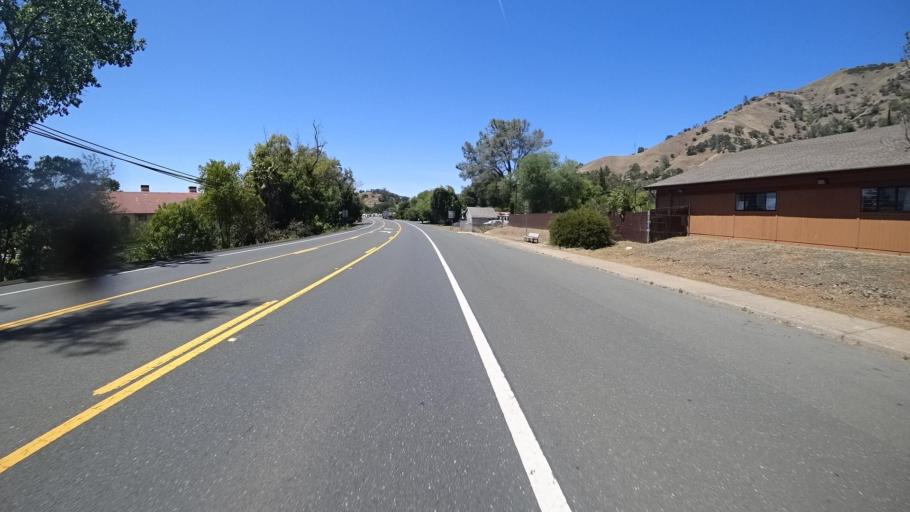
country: US
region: California
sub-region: Lake County
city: Nice
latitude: 39.1205
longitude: -122.8367
